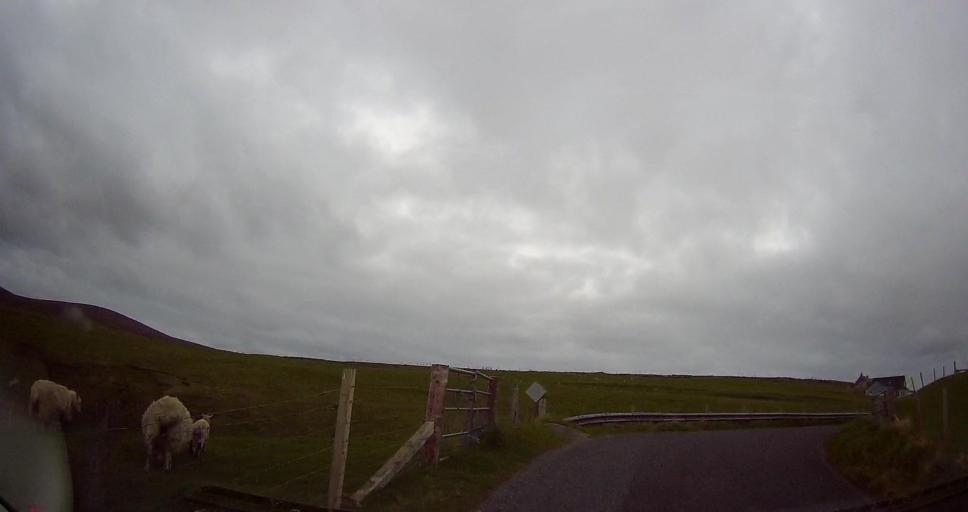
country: GB
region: Scotland
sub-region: Shetland Islands
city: Shetland
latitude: 60.8024
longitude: -0.8788
